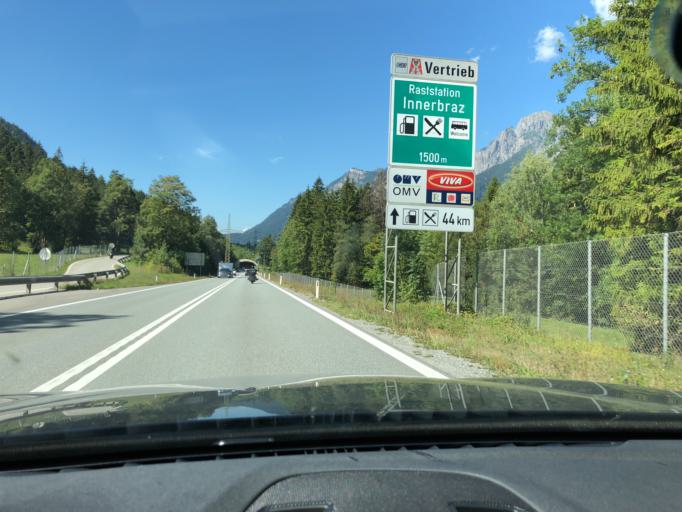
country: AT
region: Vorarlberg
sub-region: Politischer Bezirk Bludenz
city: Innerbraz
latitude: 47.1343
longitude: 9.9459
